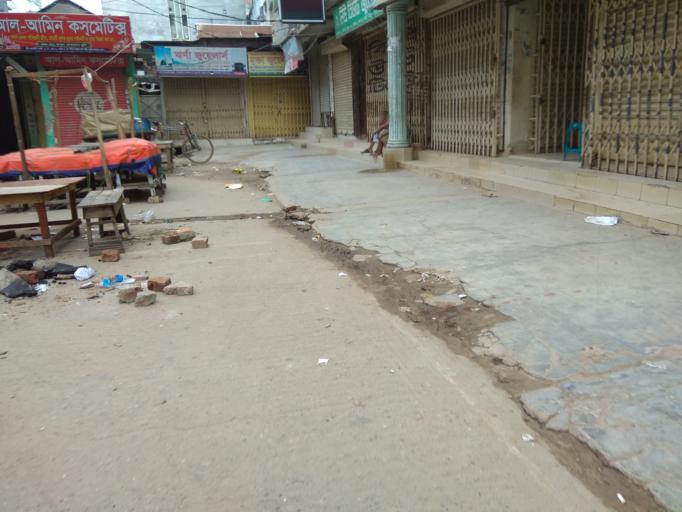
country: BD
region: Dhaka
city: Tungi
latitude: 23.8166
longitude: 90.3706
